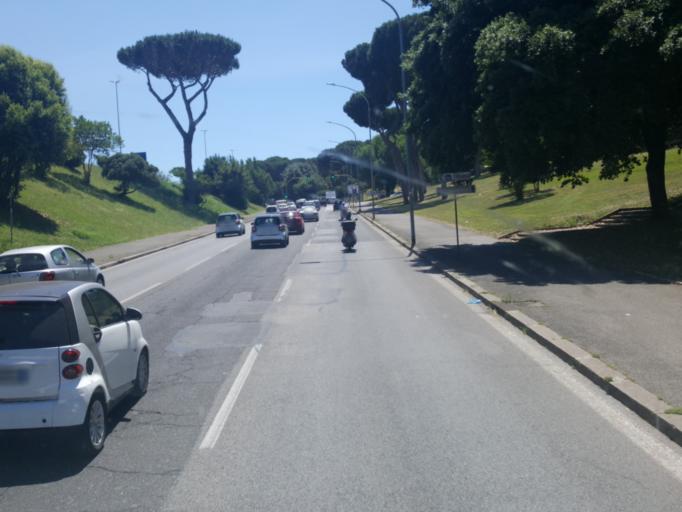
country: IT
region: Latium
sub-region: Citta metropolitana di Roma Capitale
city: Selcetta
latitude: 41.8261
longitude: 12.4651
